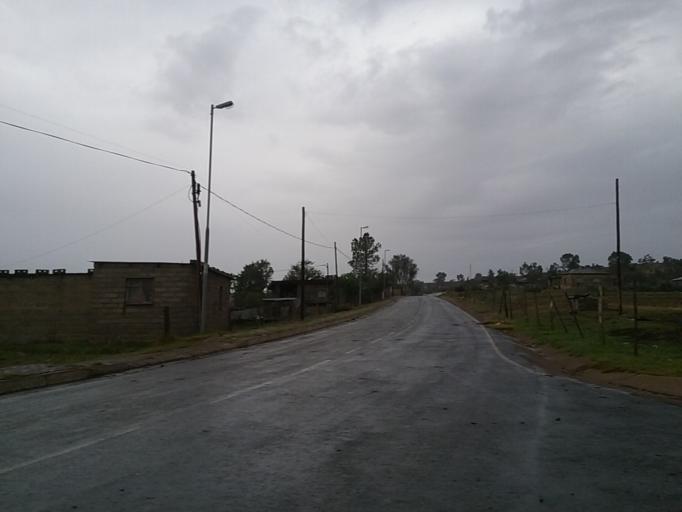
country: LS
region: Berea
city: Teyateyaneng
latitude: -29.1286
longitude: 27.7442
